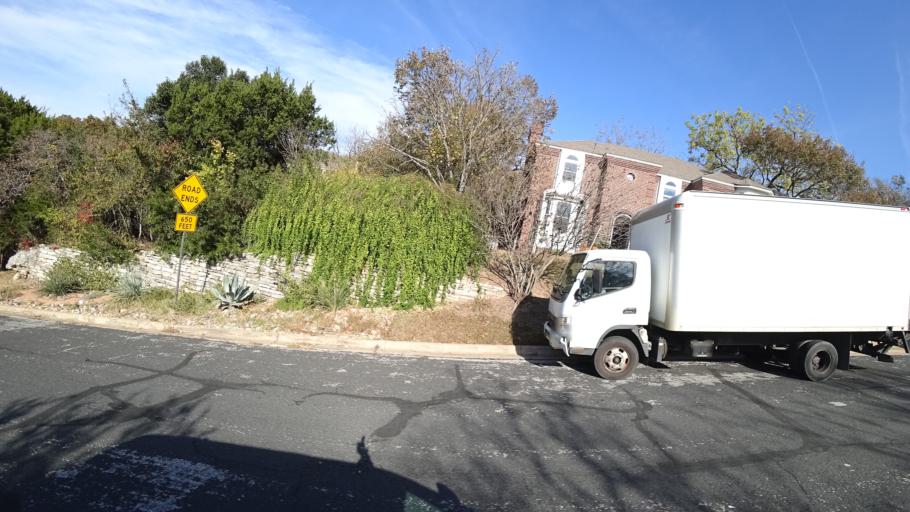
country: US
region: Texas
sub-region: Williamson County
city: Jollyville
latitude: 30.3827
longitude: -97.7553
